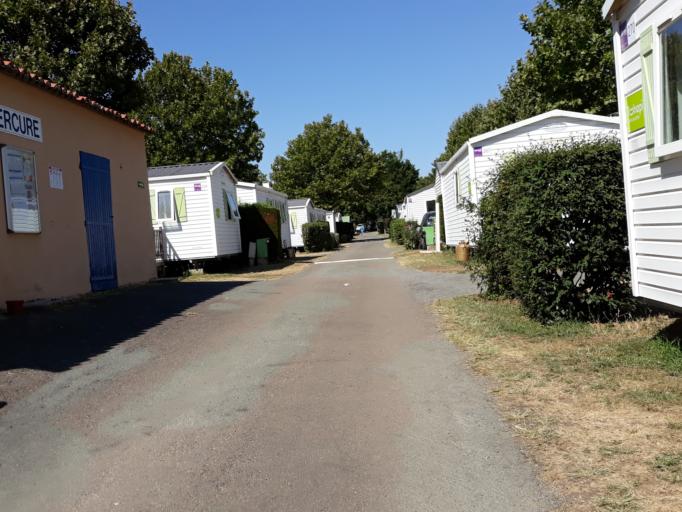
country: FR
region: Poitou-Charentes
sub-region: Departement de la Charente-Maritime
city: Saint-Laurent-de-la-Pree
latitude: 45.9870
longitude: -1.0532
